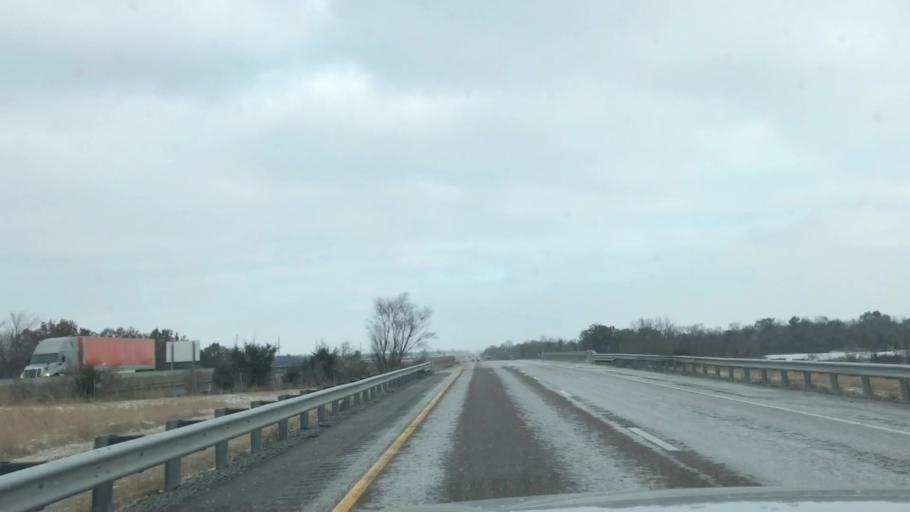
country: US
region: Illinois
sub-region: Macoupin County
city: Staunton
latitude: 38.9782
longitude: -89.7492
